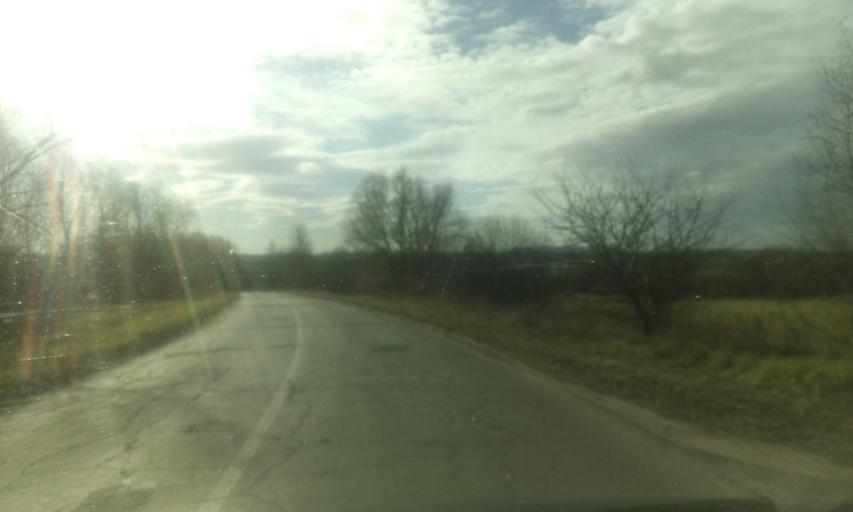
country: RU
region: Tula
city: Dubovka
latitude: 53.9525
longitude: 38.0298
